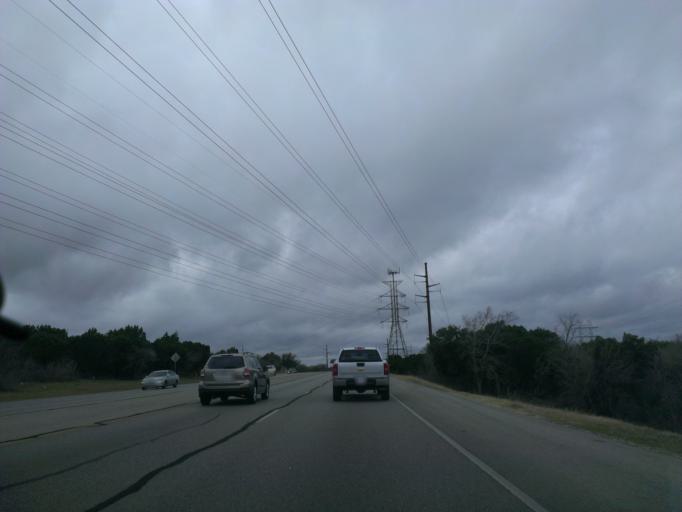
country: US
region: Texas
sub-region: Travis County
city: Hudson Bend
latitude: 30.3966
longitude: -97.8596
